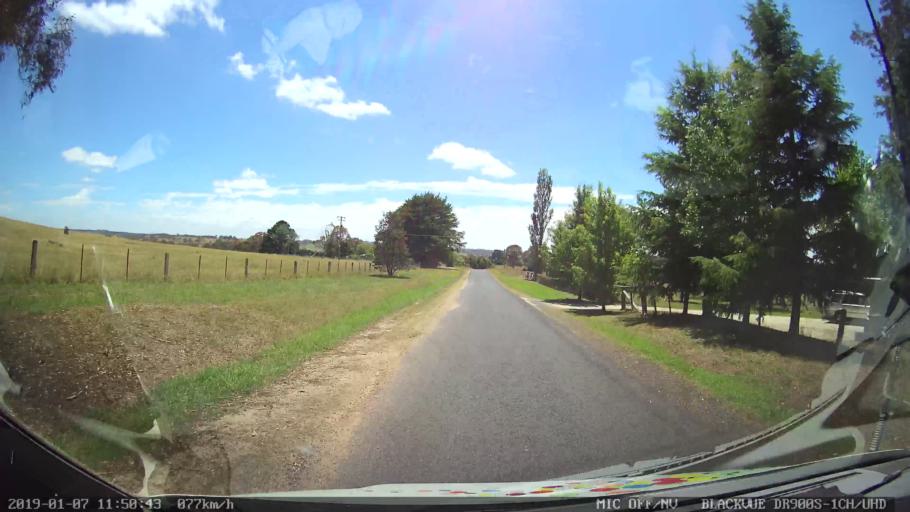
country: AU
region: New South Wales
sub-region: Guyra
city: Guyra
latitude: -30.3114
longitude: 151.6389
